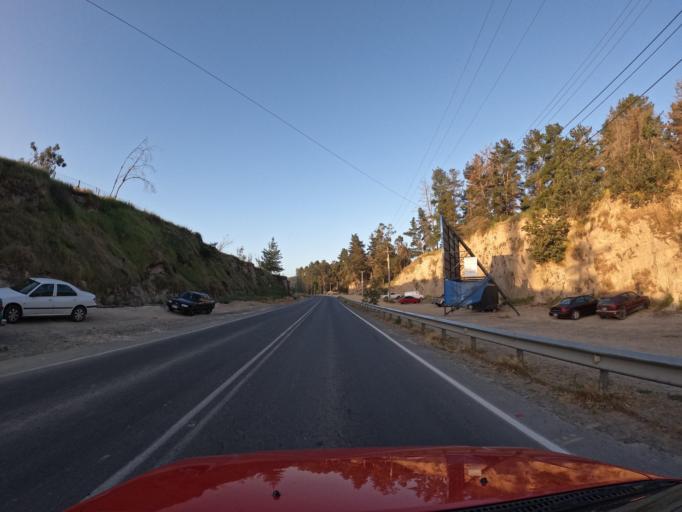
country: CL
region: O'Higgins
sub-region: Provincia de Cachapoal
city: San Vicente
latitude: -34.1457
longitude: -71.3803
